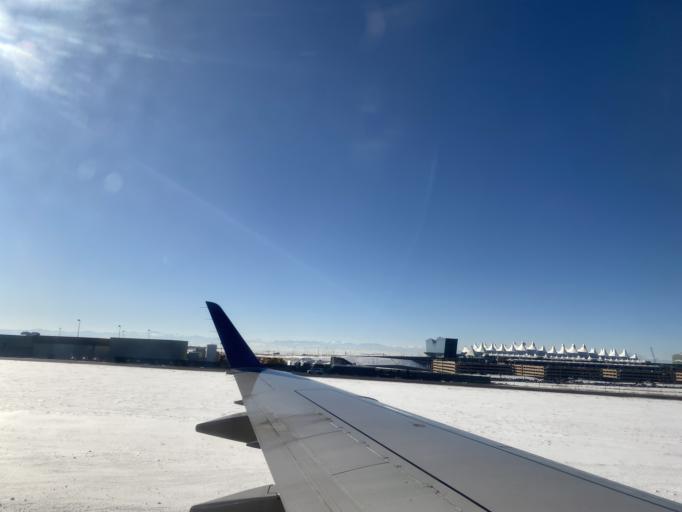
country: US
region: Colorado
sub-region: Weld County
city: Lochbuie
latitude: 39.8457
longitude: -104.6624
